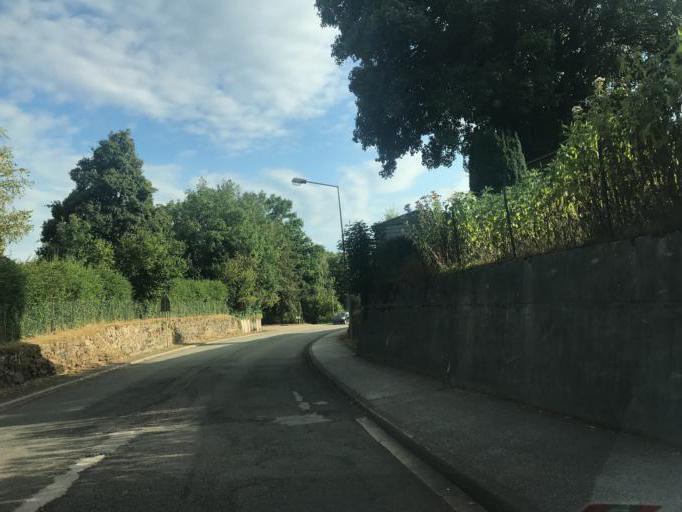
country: FR
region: Franche-Comte
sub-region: Departement du Jura
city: Saint-Lupicin
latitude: 46.3944
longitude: 5.7945
